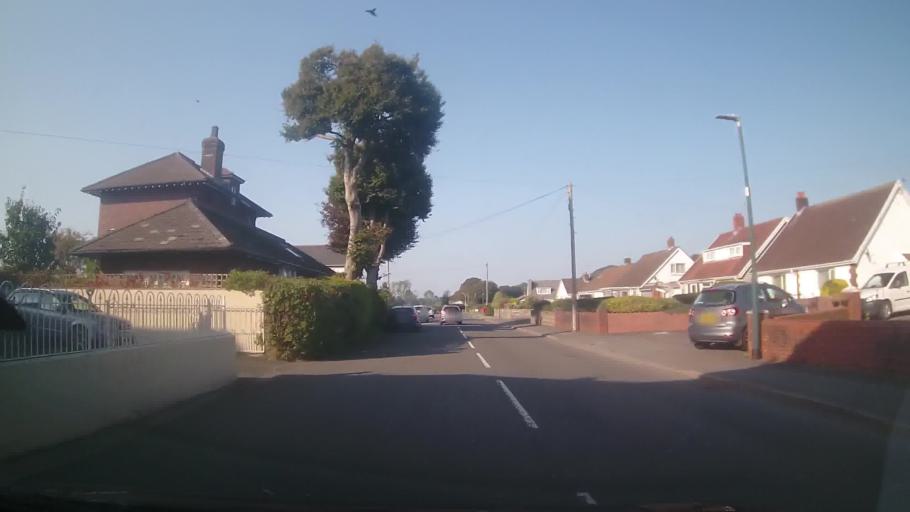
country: GB
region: Wales
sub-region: County of Ceredigion
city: Lledrod
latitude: 52.2235
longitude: -3.9325
